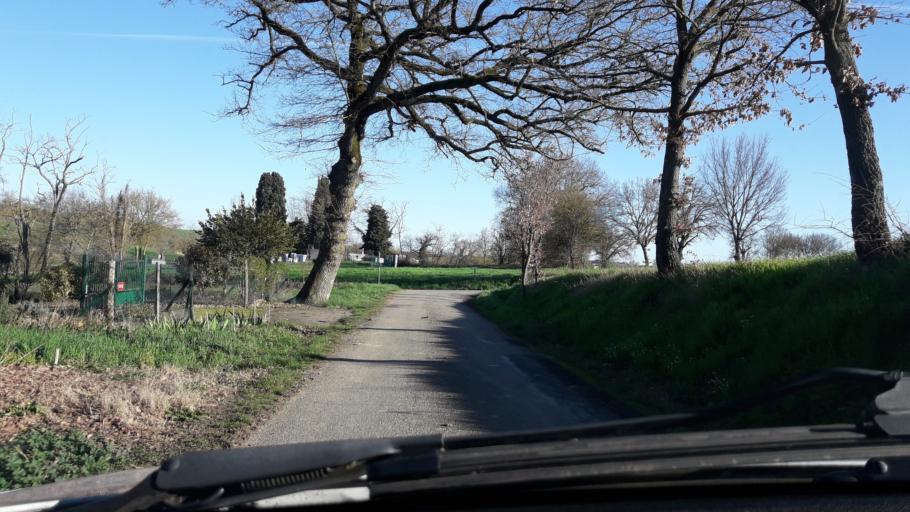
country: FR
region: Midi-Pyrenees
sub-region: Departement du Gers
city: Gimont
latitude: 43.5966
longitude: 0.9766
